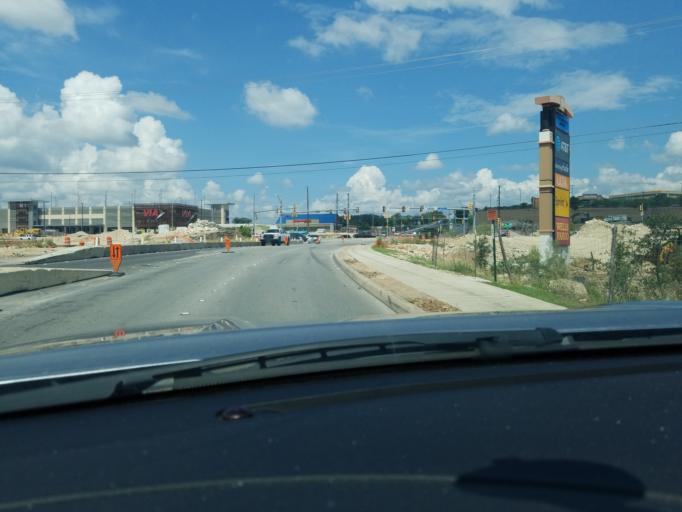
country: US
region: Texas
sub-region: Bexar County
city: Hollywood Park
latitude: 29.6487
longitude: -98.4494
